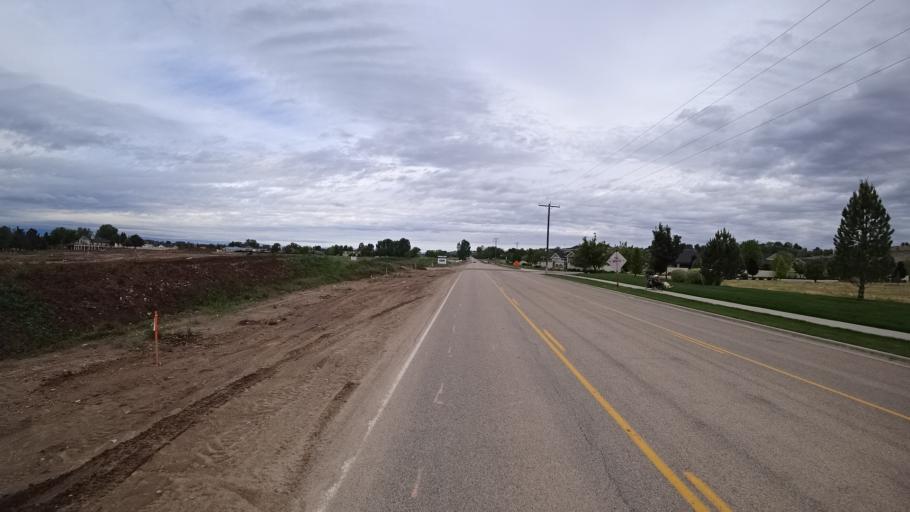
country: US
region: Idaho
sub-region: Ada County
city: Star
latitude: 43.7174
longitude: -116.4962
